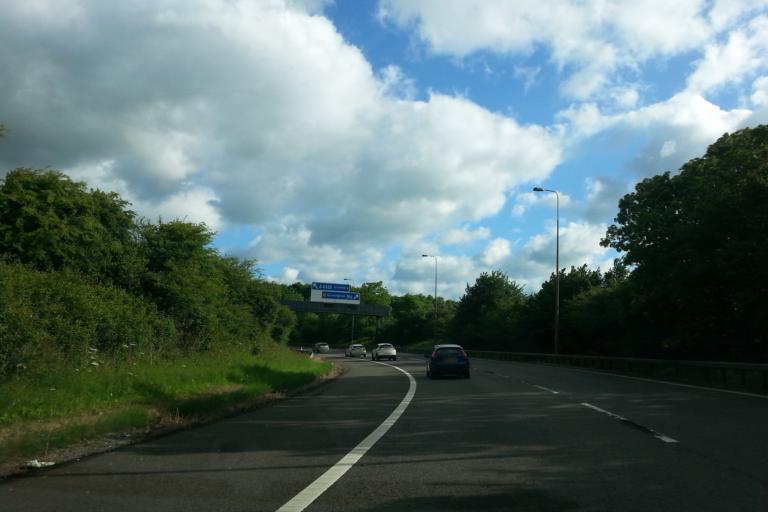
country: GB
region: England
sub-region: Warwickshire
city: Brandon
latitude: 52.4346
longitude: -1.4177
